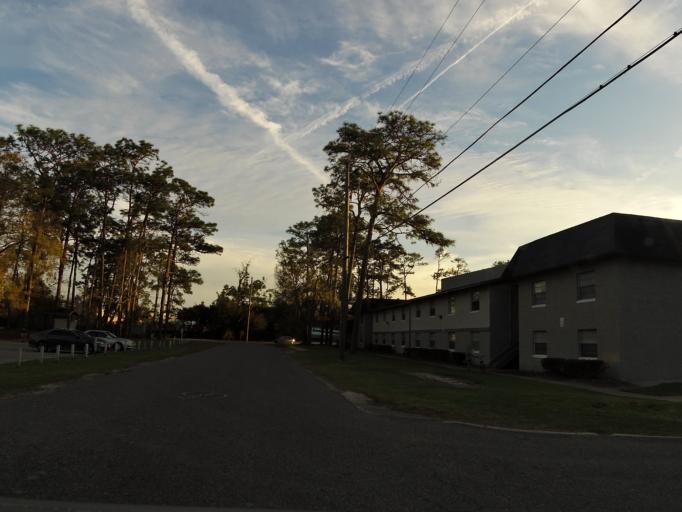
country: US
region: Florida
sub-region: Duval County
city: Jacksonville
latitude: 30.2939
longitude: -81.6364
